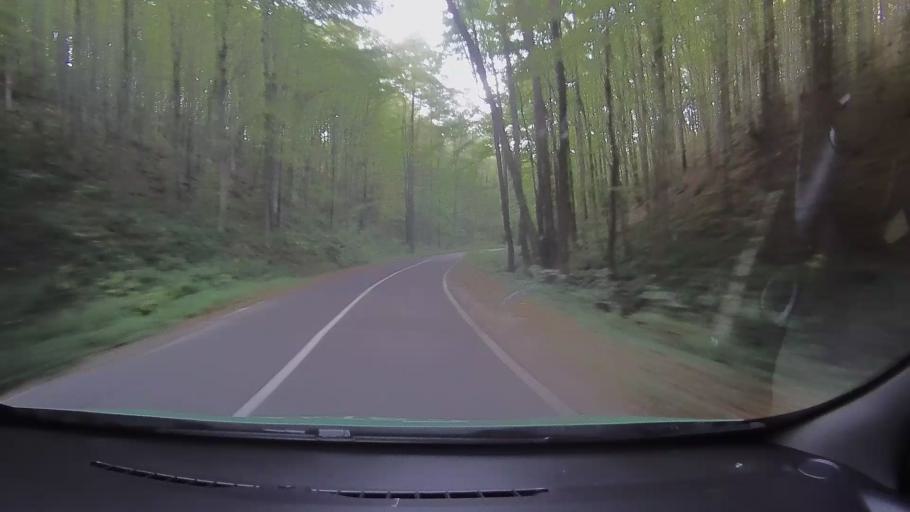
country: RO
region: Timis
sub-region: Comuna Nadrag
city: Nadrag
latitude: 45.6831
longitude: 22.1566
